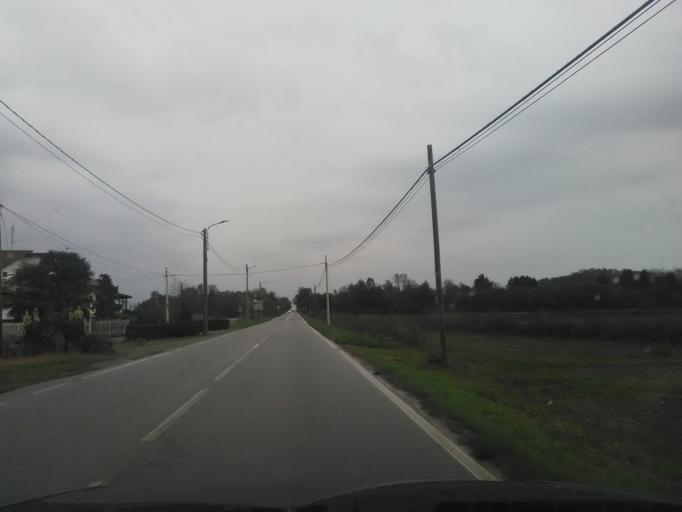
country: IT
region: Piedmont
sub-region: Provincia di Vercelli
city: Carisio
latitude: 45.4152
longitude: 8.2039
